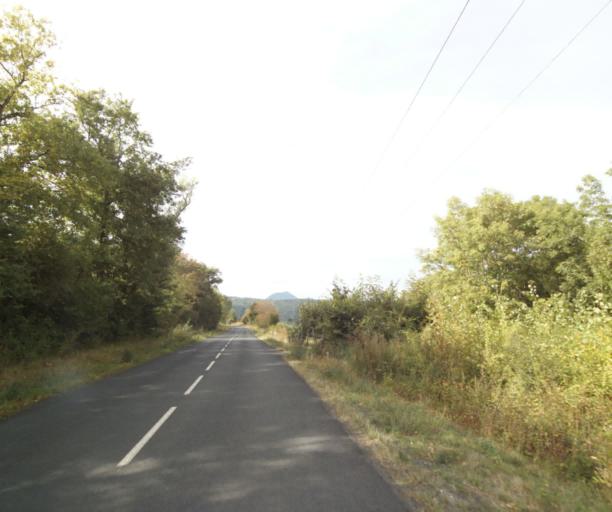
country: FR
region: Auvergne
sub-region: Departement du Puy-de-Dome
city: Romagnat
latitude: 45.7129
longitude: 3.0859
